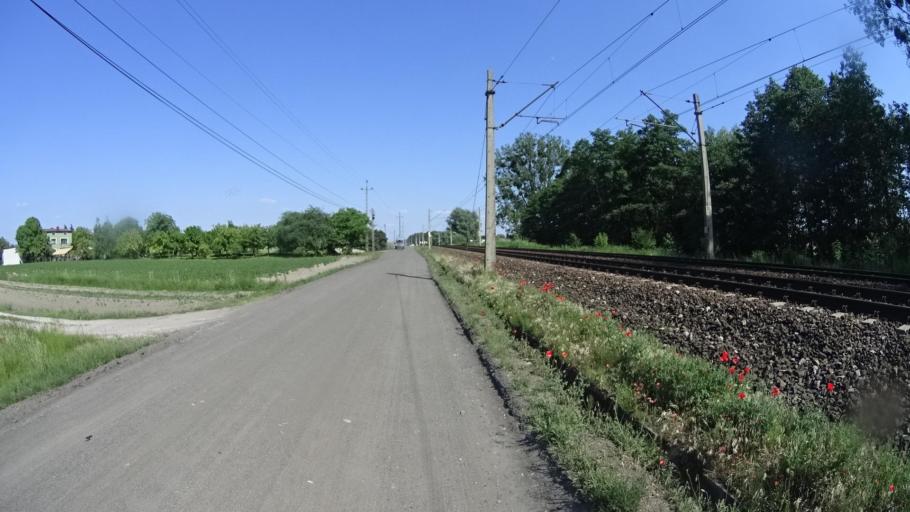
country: PL
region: Masovian Voivodeship
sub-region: Powiat warszawski zachodni
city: Bieniewice
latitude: 52.1865
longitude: 20.5584
